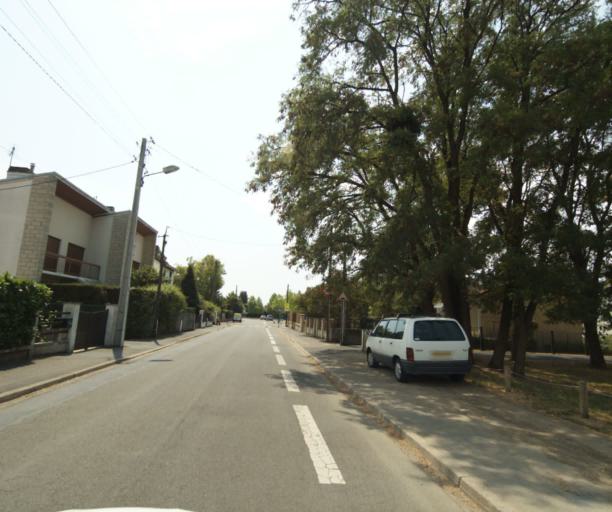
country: FR
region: Ile-de-France
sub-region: Departement des Yvelines
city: Conflans-Sainte-Honorine
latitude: 48.9991
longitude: 2.0846
